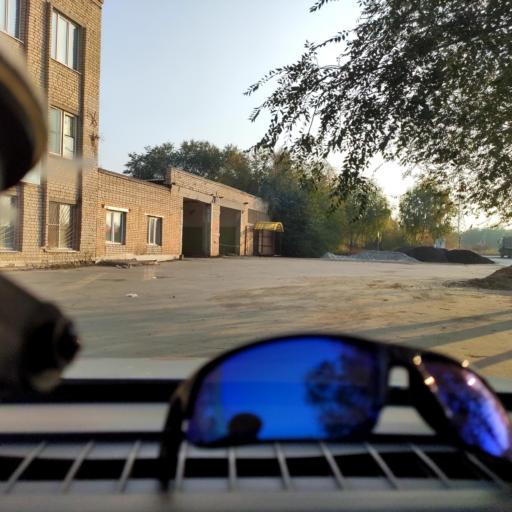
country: RU
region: Samara
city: Chapayevsk
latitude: 52.9513
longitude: 49.7004
